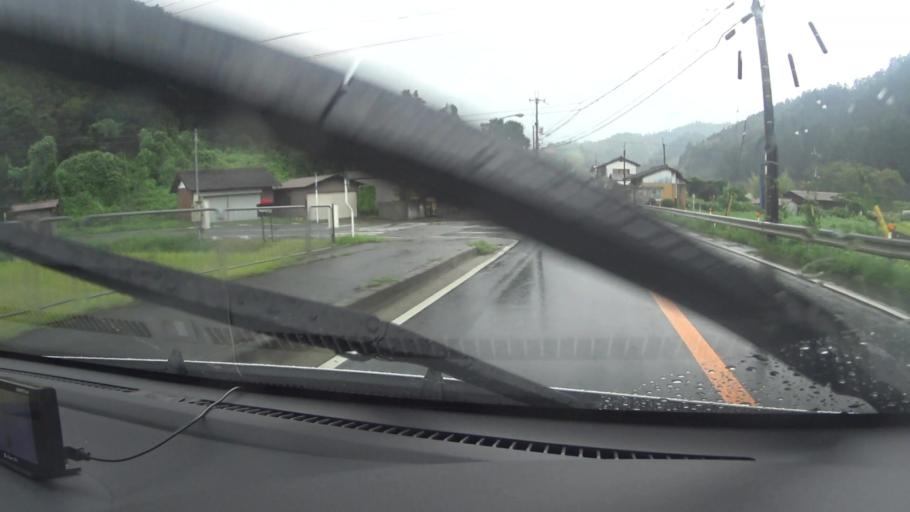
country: JP
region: Kyoto
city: Ayabe
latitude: 35.2099
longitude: 135.3506
